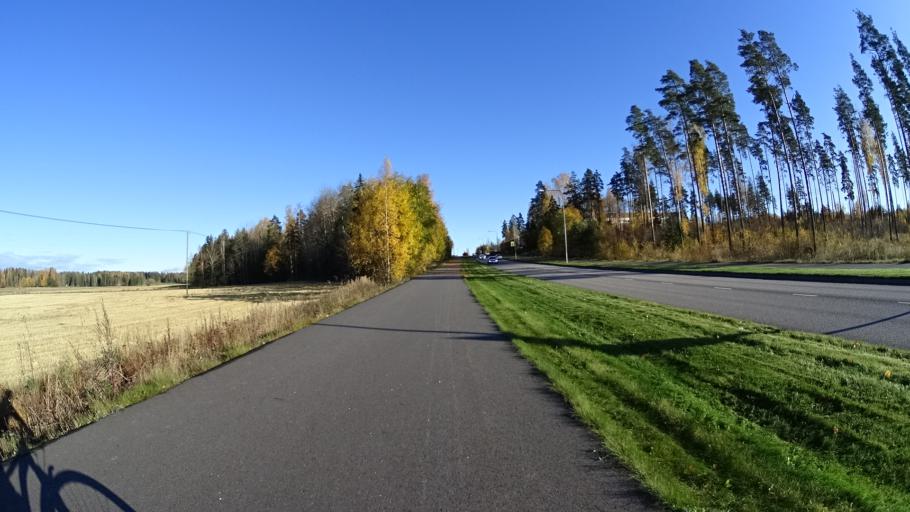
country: FI
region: Uusimaa
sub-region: Helsinki
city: Kauniainen
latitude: 60.2553
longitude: 24.7129
